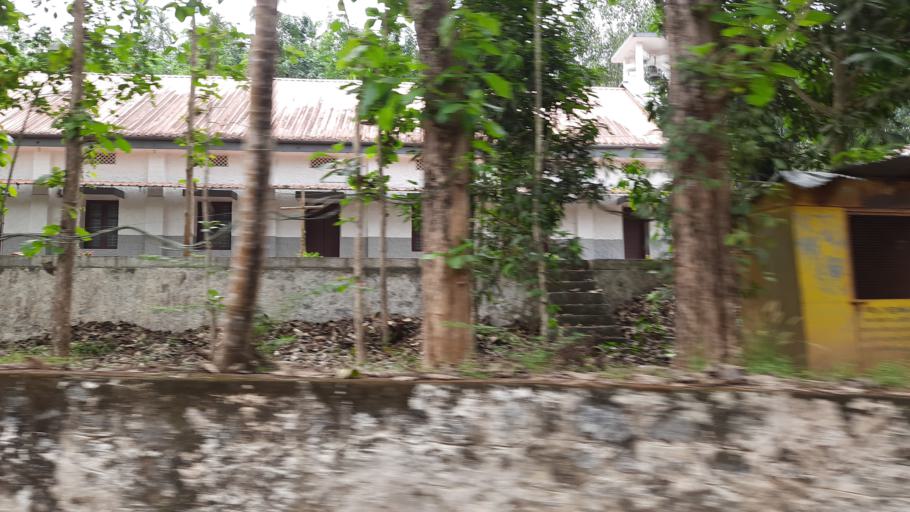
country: IN
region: Kerala
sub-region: Kottayam
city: Lalam
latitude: 9.8208
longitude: 76.7505
